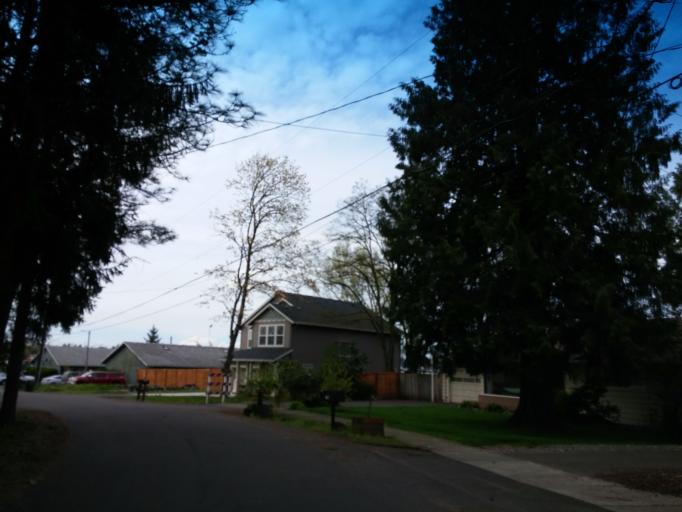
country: US
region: Oregon
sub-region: Washington County
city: Cedar Mill
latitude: 45.5271
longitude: -122.8120
